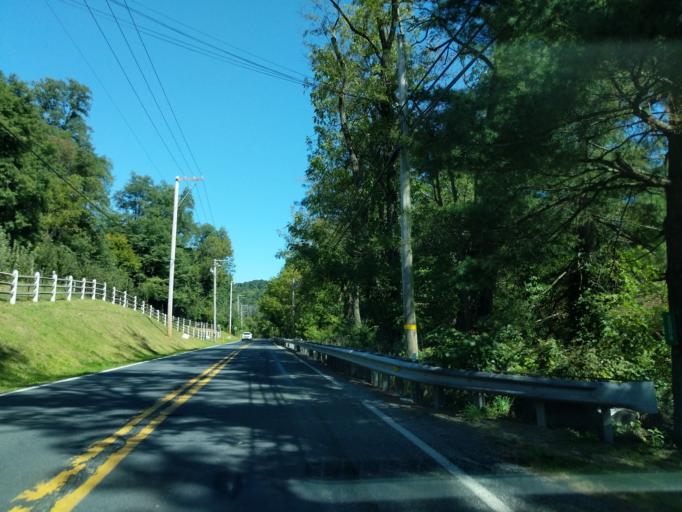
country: US
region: Pennsylvania
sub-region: Bucks County
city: Spinnerstown
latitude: 40.4907
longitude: -75.4466
